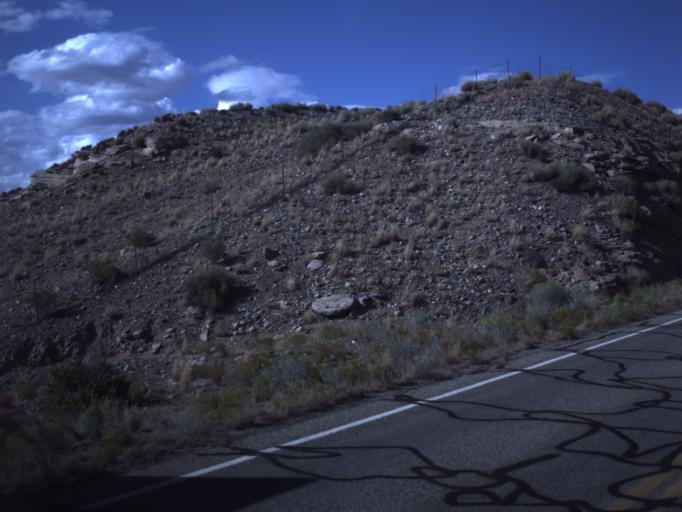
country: US
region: Utah
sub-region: San Juan County
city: Blanding
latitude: 37.2672
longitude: -109.3028
